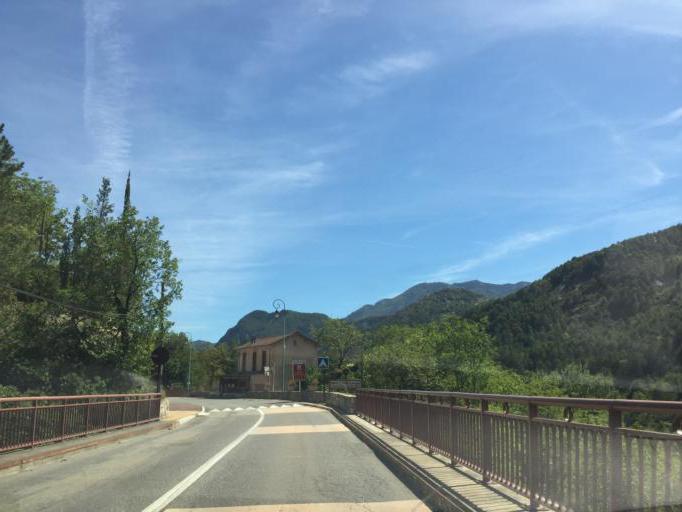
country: FR
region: Provence-Alpes-Cote d'Azur
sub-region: Departement des Alpes-Maritimes
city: Gilette
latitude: 43.9647
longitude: 7.1523
